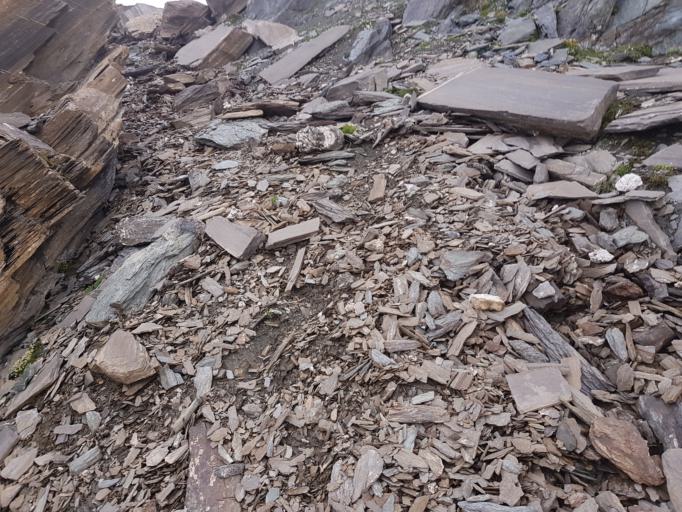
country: IT
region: Piedmont
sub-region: Provincia di Cuneo
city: Pleyne
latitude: 44.6196
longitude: 6.9502
